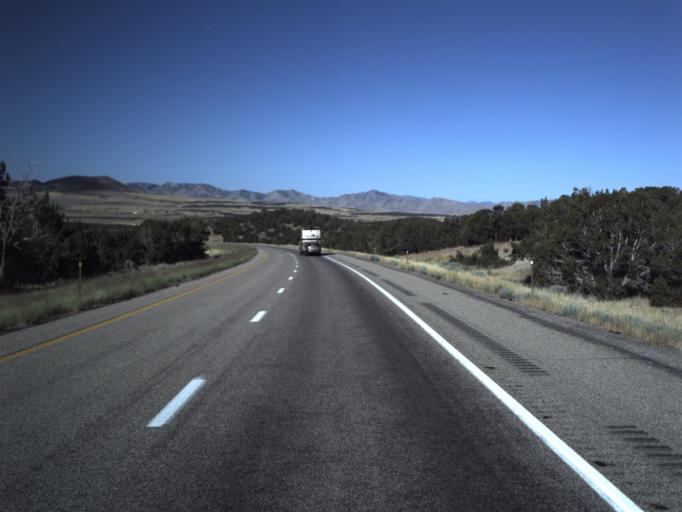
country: US
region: Utah
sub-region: Beaver County
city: Beaver
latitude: 38.6051
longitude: -112.5472
